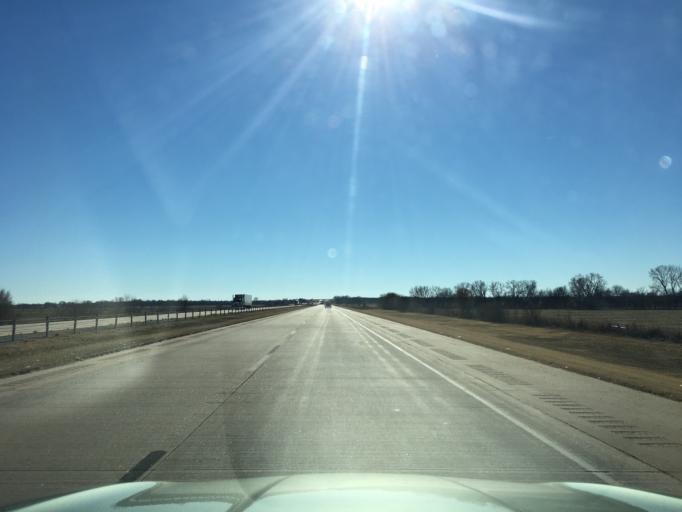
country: US
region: Oklahoma
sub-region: Noble County
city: Perry
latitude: 36.4749
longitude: -97.3272
